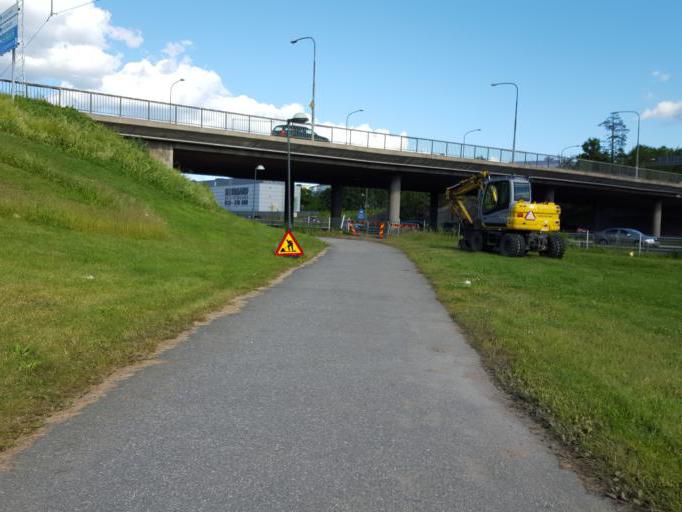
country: SE
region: Stockholm
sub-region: Huddinge Kommun
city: Segeltorp
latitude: 59.2879
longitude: 17.9472
